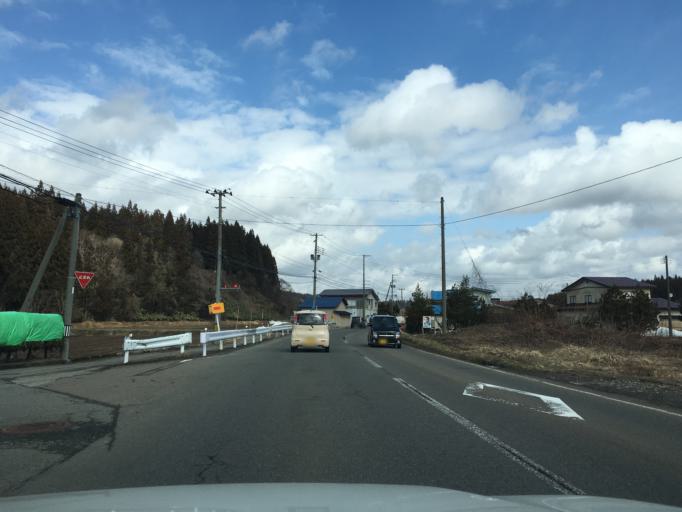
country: JP
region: Akita
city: Takanosu
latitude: 40.0336
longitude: 140.2751
